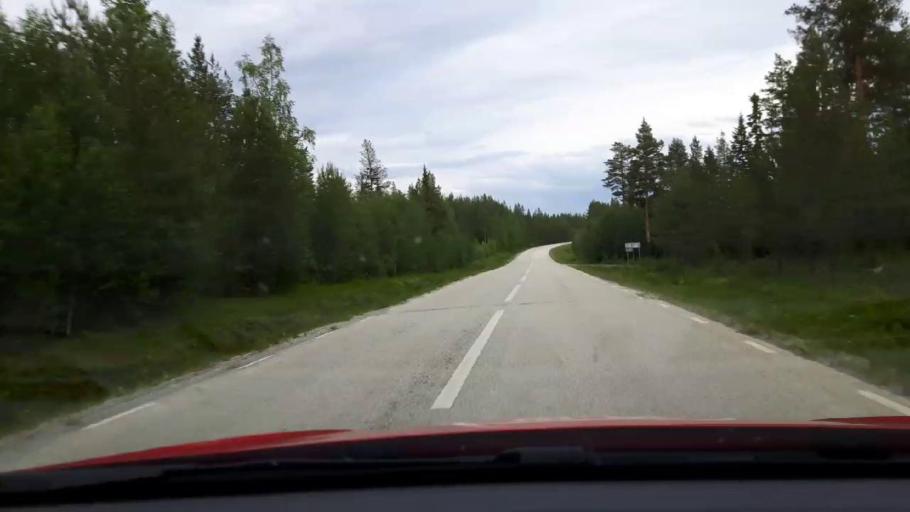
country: SE
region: Jaemtland
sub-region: Bergs Kommun
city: Hoverberg
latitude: 62.7180
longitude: 13.9189
